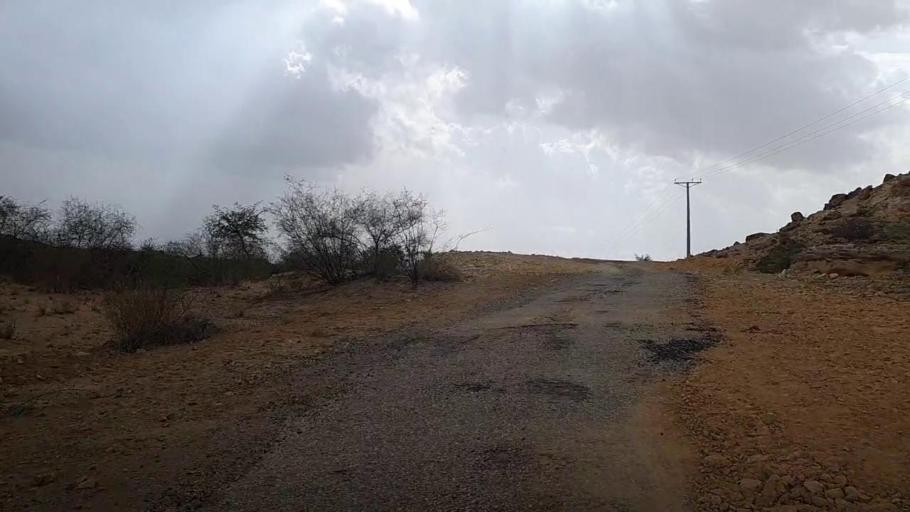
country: PK
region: Sindh
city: Jamshoro
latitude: 25.3936
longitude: 67.6844
